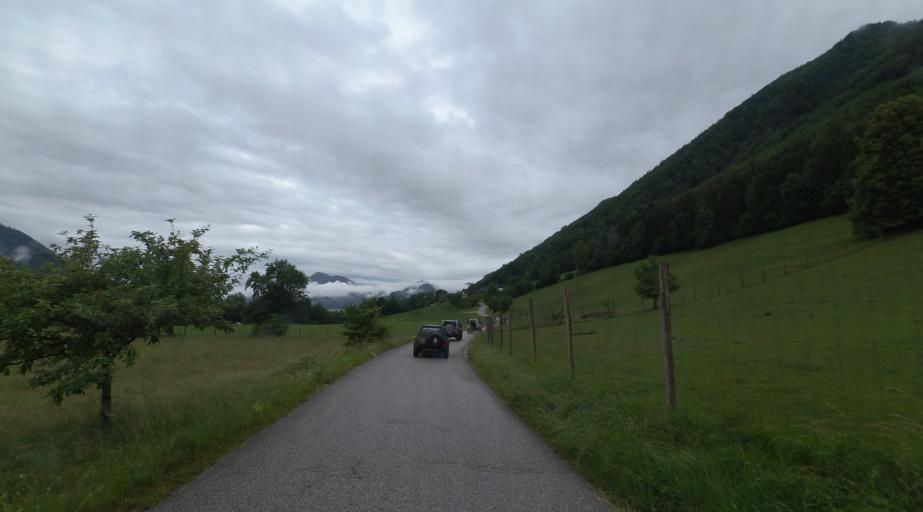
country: AT
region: Upper Austria
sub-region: Politischer Bezirk Steyr-Land
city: Ternberg
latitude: 47.8940
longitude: 14.2952
